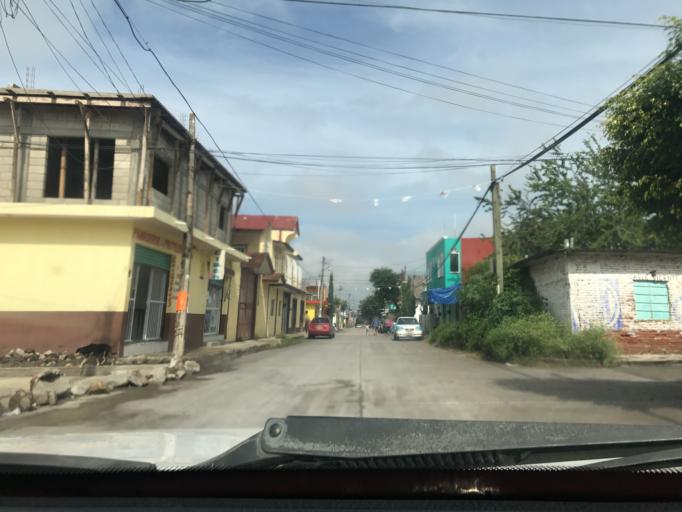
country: MX
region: Morelos
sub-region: Yecapixtla
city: Mixtlalcingo
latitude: 18.8024
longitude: -98.9094
